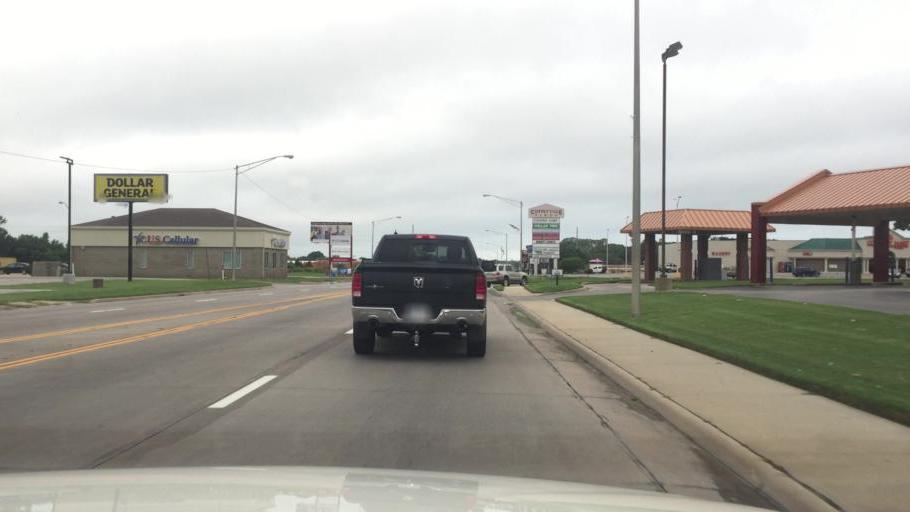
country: US
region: Kansas
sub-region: Montgomery County
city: Coffeyville
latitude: 37.0333
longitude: -95.6391
